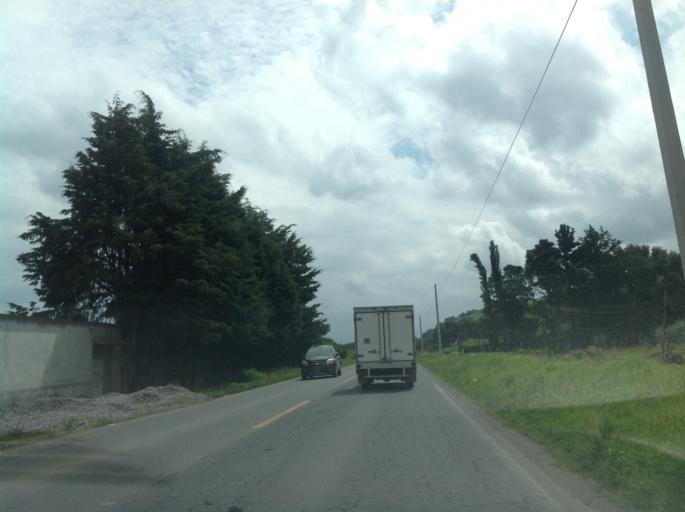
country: MX
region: Mexico
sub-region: Rayon
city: Colonia Emiliano Zapata
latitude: 19.1108
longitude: -99.5698
